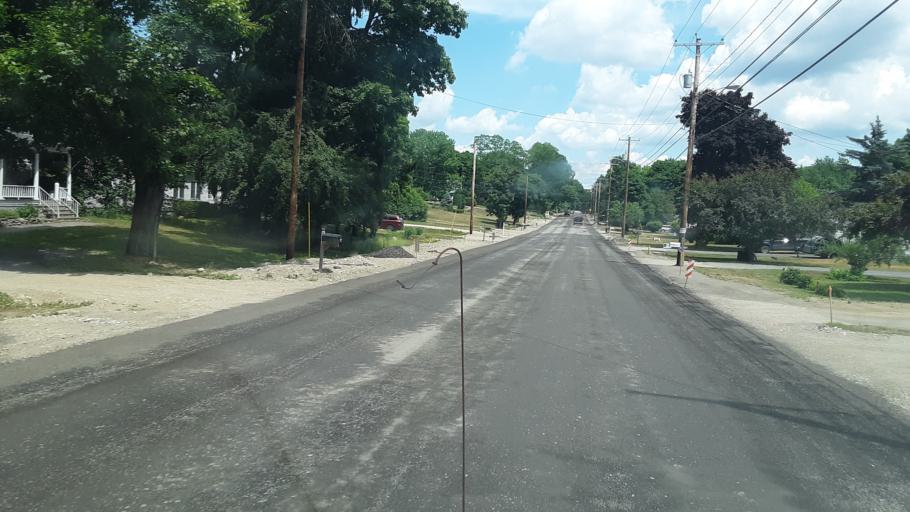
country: US
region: Maine
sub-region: Penobscot County
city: Hampden
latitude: 44.7559
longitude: -68.8195
